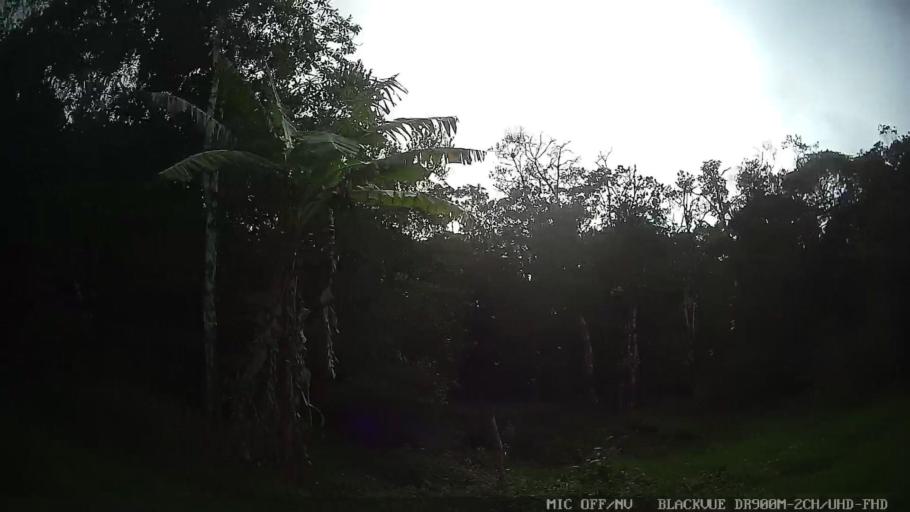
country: BR
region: Sao Paulo
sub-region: Peruibe
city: Peruibe
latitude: -24.2315
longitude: -46.9117
